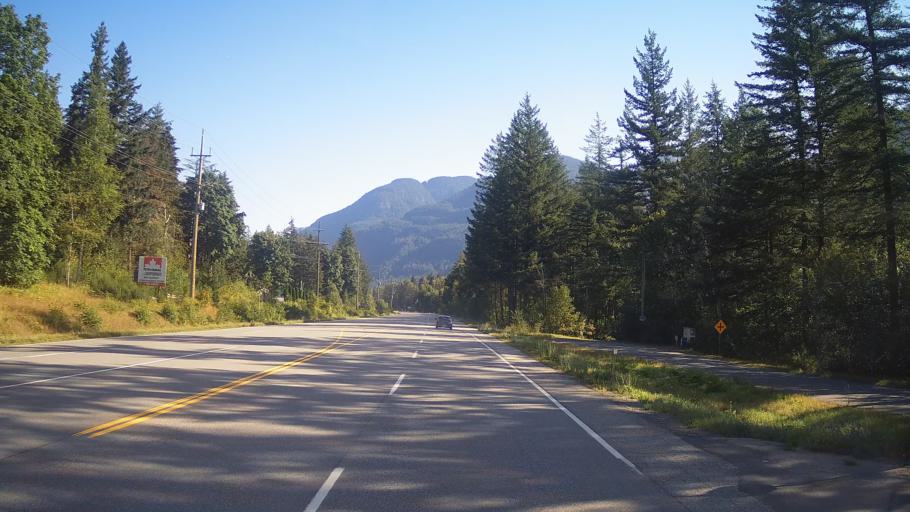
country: CA
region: British Columbia
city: Hope
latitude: 49.4756
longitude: -121.4257
